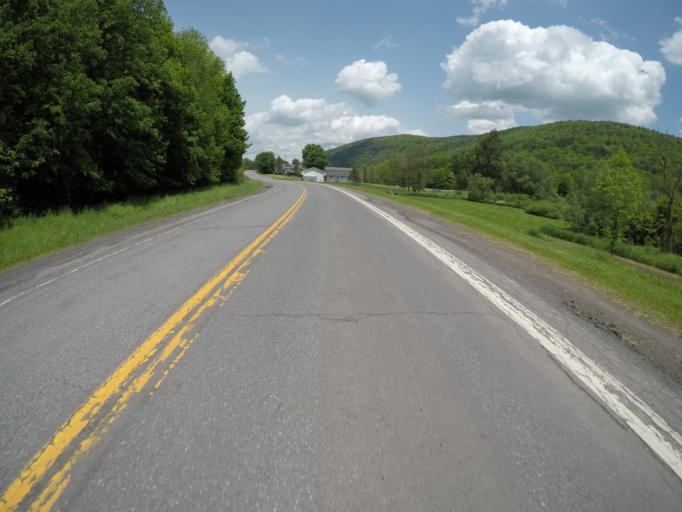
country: US
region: New York
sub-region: Delaware County
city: Stamford
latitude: 42.1610
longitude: -74.6227
